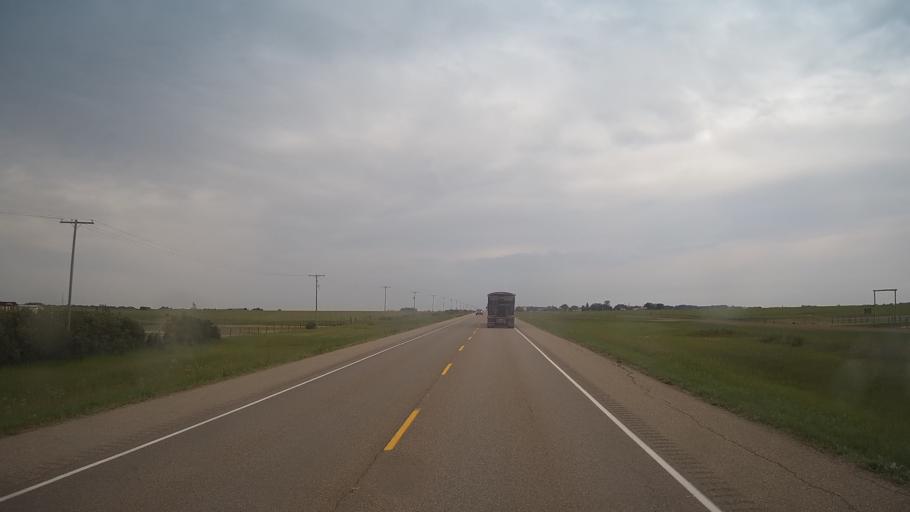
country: CA
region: Saskatchewan
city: Langham
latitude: 52.1290
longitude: -107.1793
